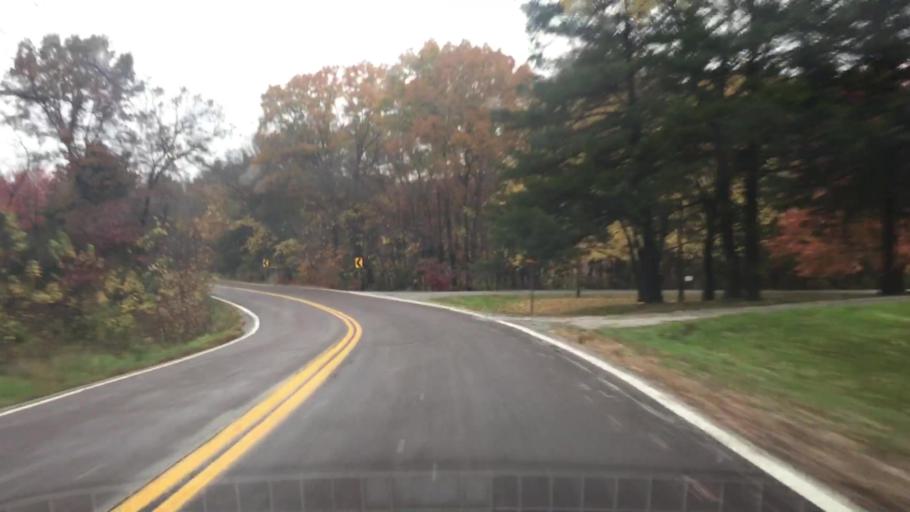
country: US
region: Missouri
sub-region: Boone County
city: Columbia
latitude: 38.8664
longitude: -92.3171
